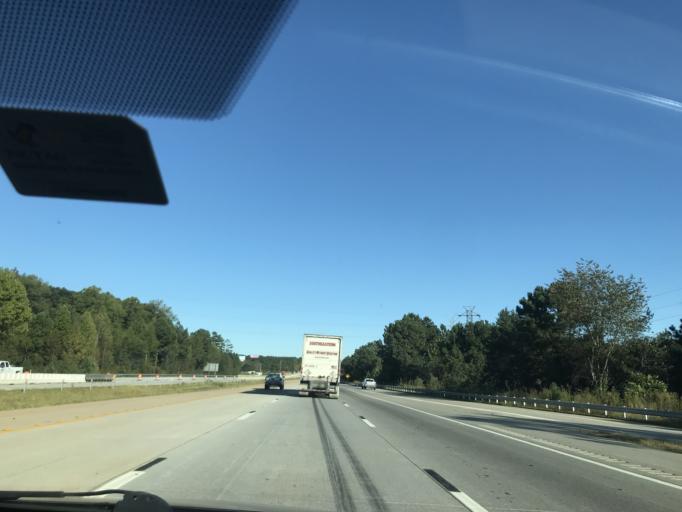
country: US
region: South Carolina
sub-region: Spartanburg County
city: Valley Falls
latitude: 35.0126
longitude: -81.9547
